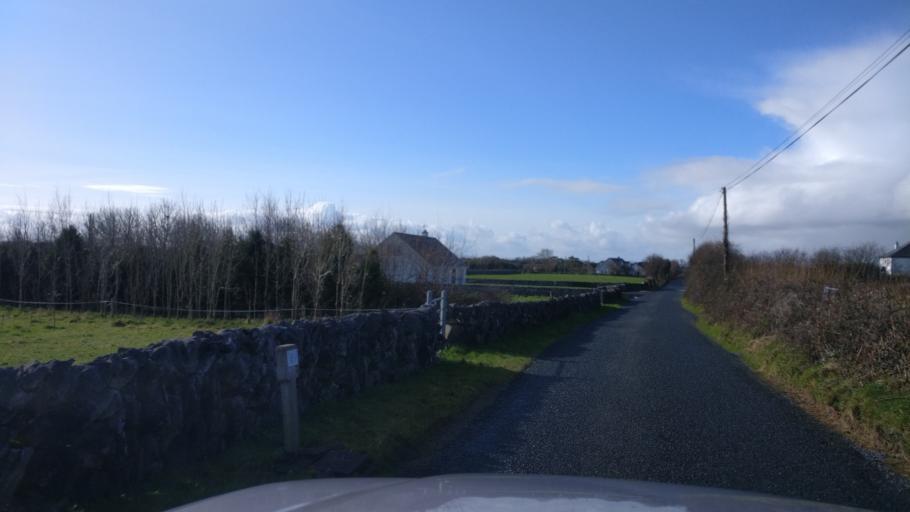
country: IE
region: Connaught
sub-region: County Galway
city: Athenry
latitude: 53.2427
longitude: -8.7728
